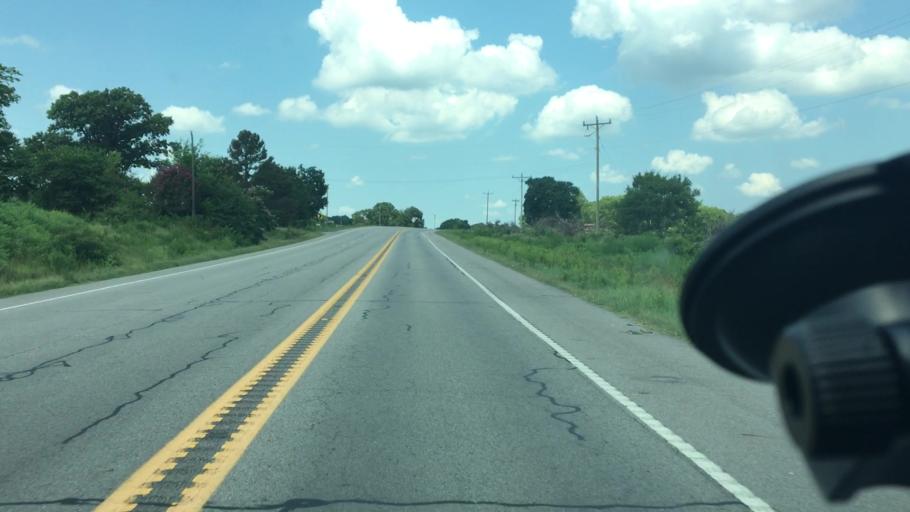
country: US
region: Arkansas
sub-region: Logan County
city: Paris
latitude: 35.2988
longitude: -93.8254
